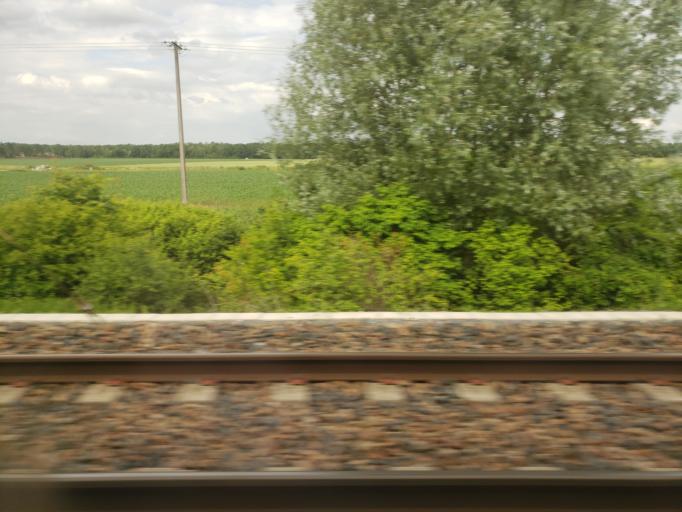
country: FR
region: Ile-de-France
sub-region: Departement de Seine-et-Marne
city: Serris
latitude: 48.8198
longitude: 2.7826
